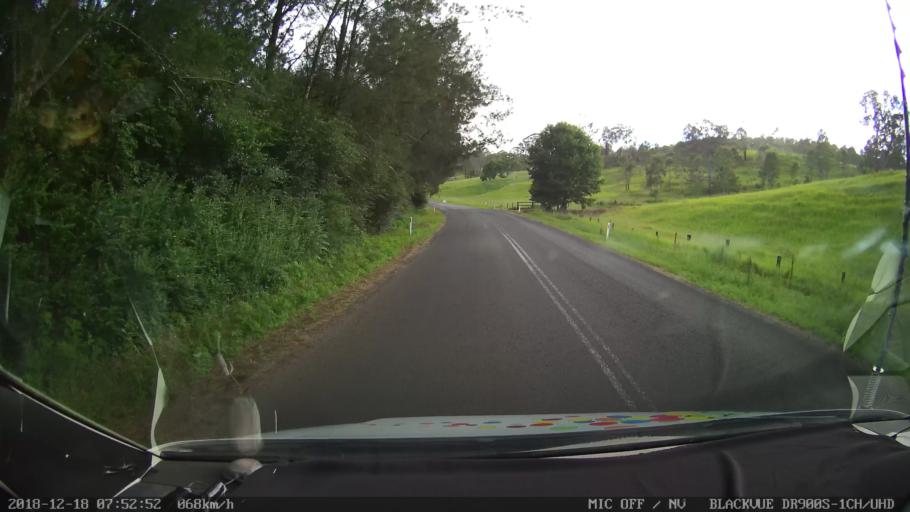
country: AU
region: New South Wales
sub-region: Kyogle
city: Kyogle
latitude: -28.4244
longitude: 152.5815
